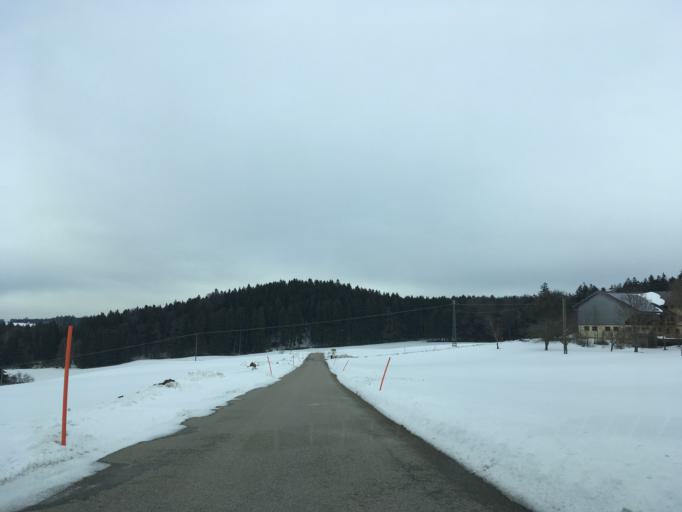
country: DE
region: Bavaria
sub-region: Upper Bavaria
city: Schnaitsee
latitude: 48.0347
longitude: 12.3613
